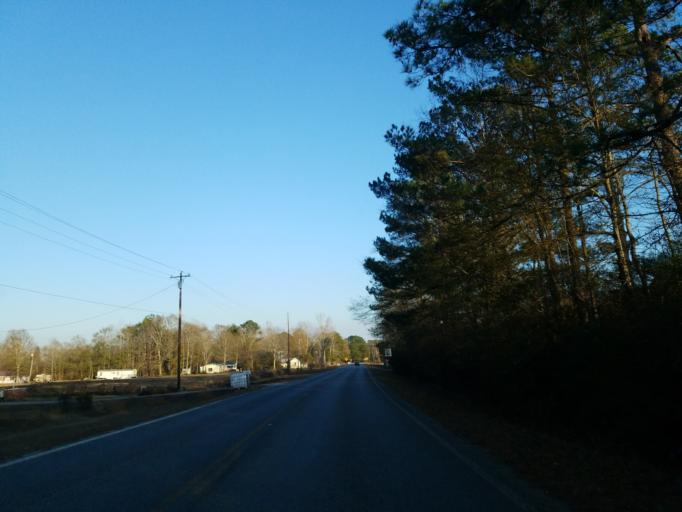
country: US
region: Mississippi
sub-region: Clarke County
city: Stonewall
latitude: 32.1703
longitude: -88.8387
